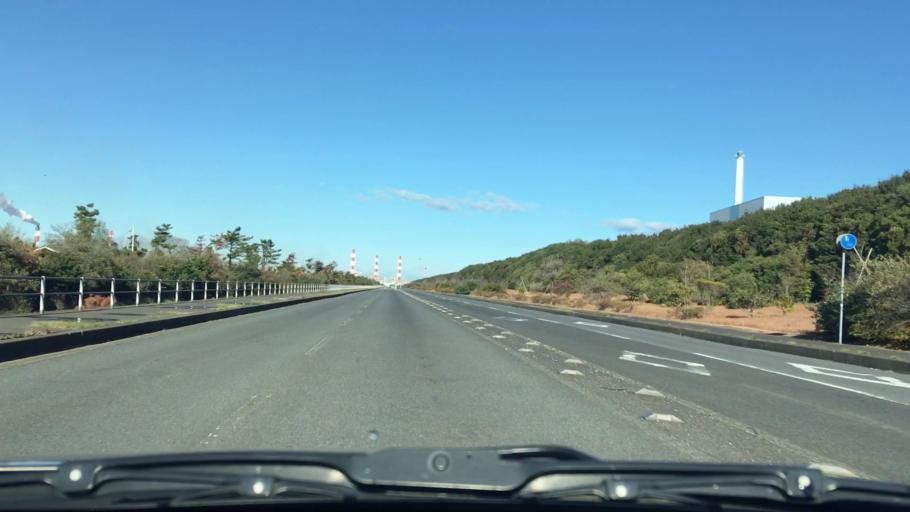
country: JP
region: Chiba
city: Omigawa
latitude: 35.8738
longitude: 140.7346
